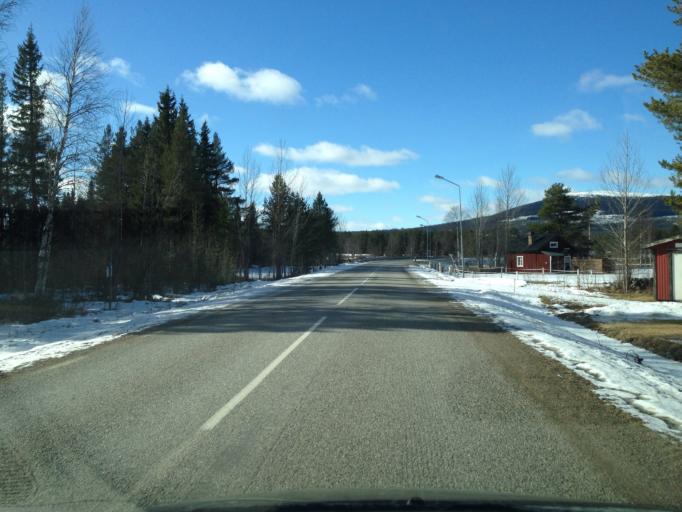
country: SE
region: Jaemtland
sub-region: Harjedalens Kommun
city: Sveg
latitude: 62.1548
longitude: 13.8805
